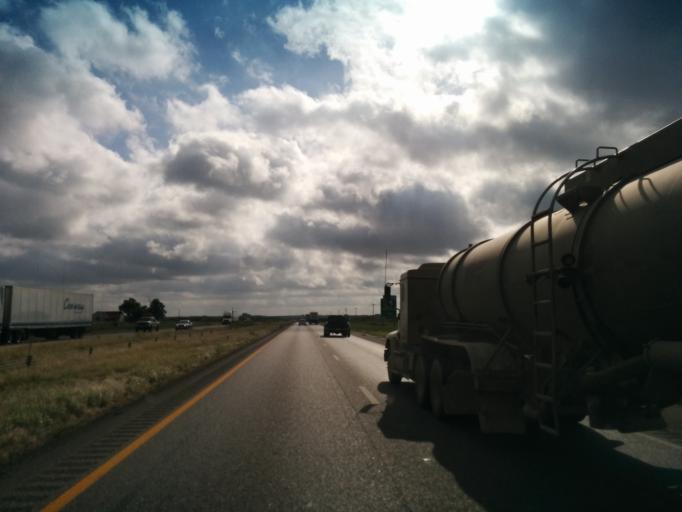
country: US
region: Texas
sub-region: Guadalupe County
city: Marion
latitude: 29.5220
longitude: -98.1307
